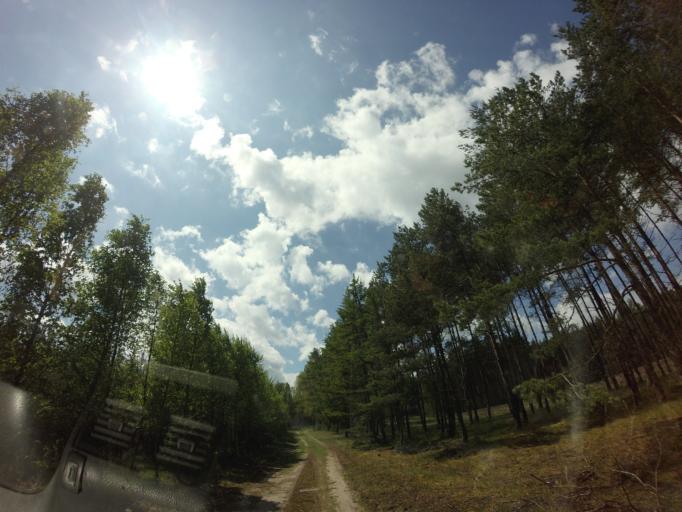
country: PL
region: West Pomeranian Voivodeship
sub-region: Powiat drawski
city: Kalisz Pomorski
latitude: 53.1806
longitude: 15.9374
